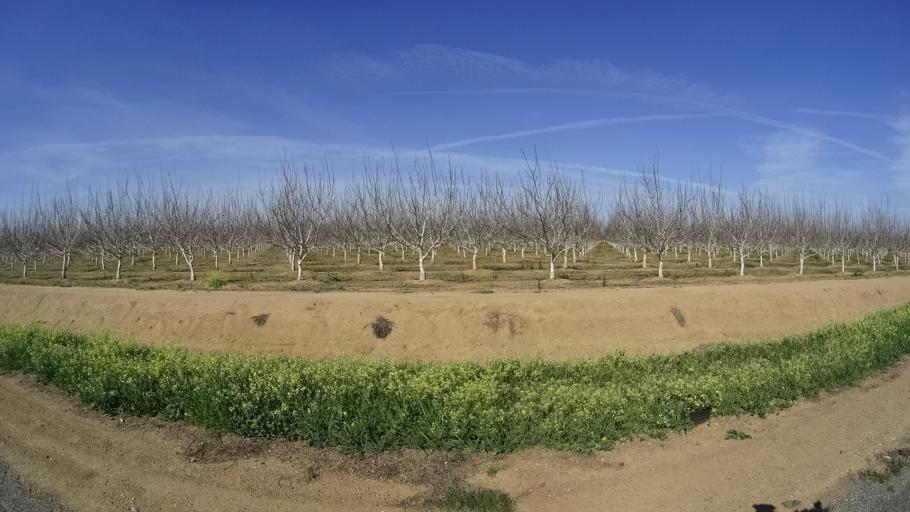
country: US
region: California
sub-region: Glenn County
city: Willows
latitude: 39.6223
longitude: -122.2130
